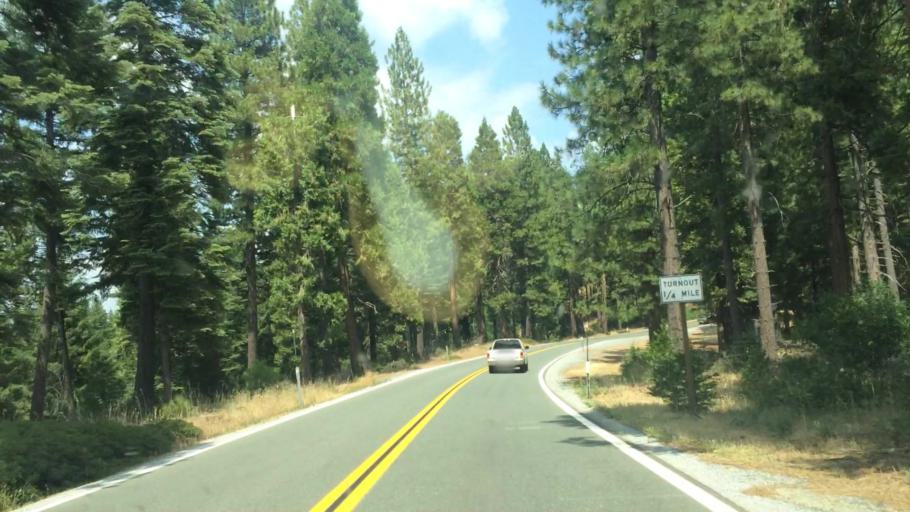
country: US
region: California
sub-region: Amador County
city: Pioneer
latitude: 38.5214
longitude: -120.4514
